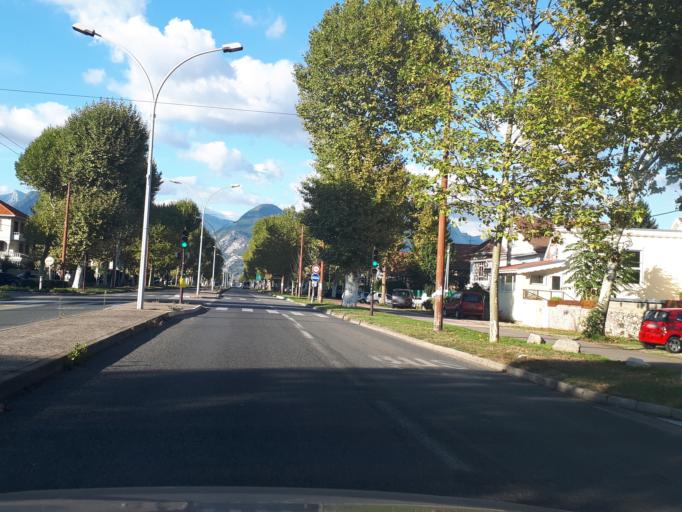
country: FR
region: Rhone-Alpes
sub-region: Departement de l'Isere
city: Grenoble
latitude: 45.1538
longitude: 5.7076
